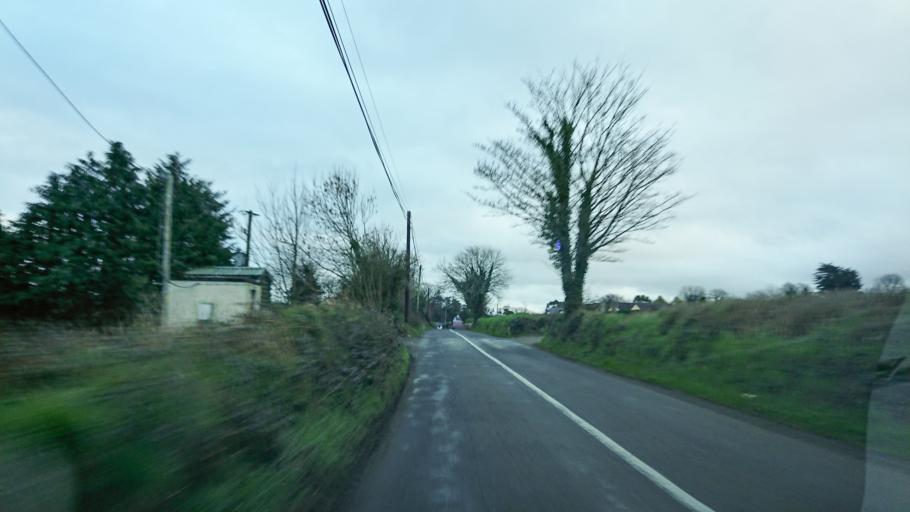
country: IE
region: Munster
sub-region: Waterford
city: Portlaw
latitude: 52.1917
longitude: -7.4151
